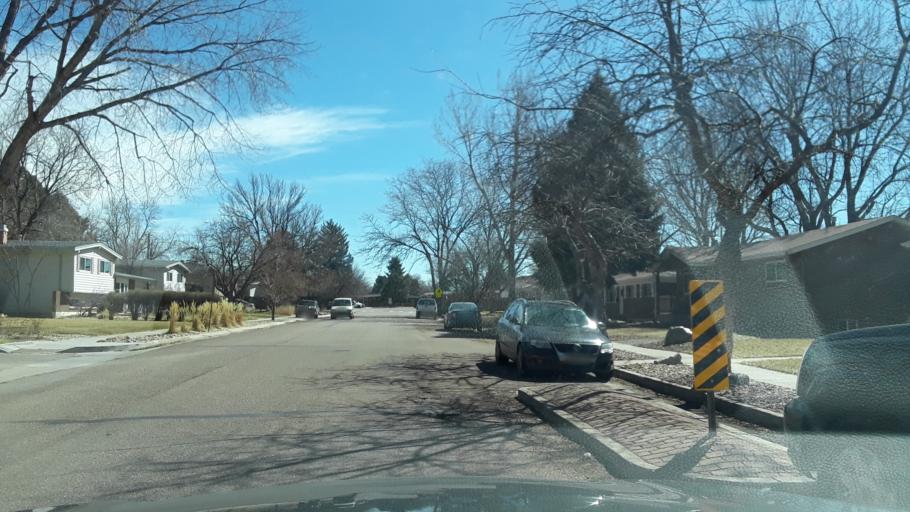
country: US
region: Colorado
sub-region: El Paso County
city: Colorado Springs
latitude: 38.8682
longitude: -104.8077
